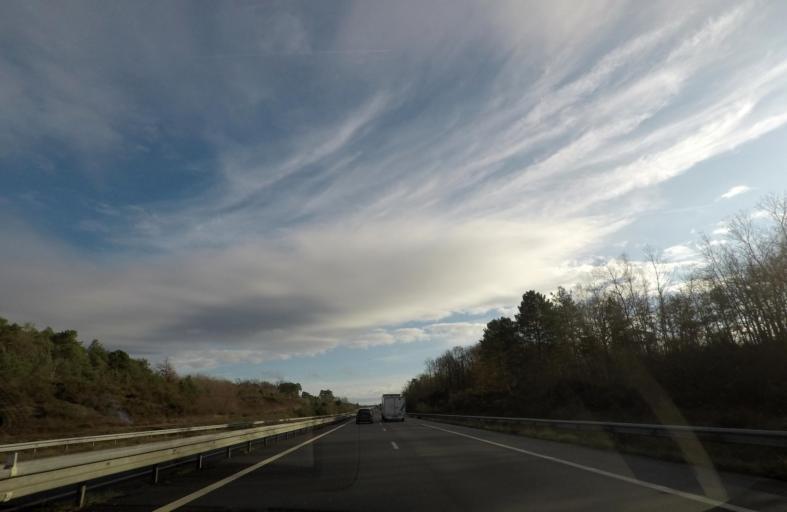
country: FR
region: Centre
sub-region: Departement du Loir-et-Cher
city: Villefranche-sur-Cher
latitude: 47.3143
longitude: 1.8143
